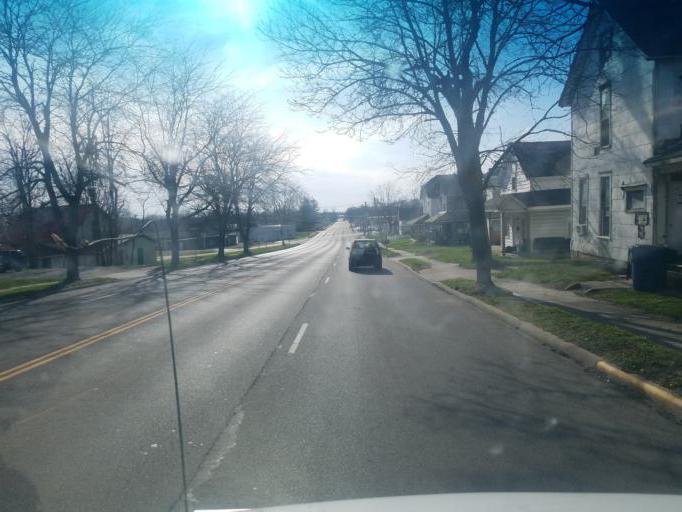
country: US
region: Ohio
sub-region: Logan County
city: Bellefontaine
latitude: 40.3631
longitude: -83.7655
